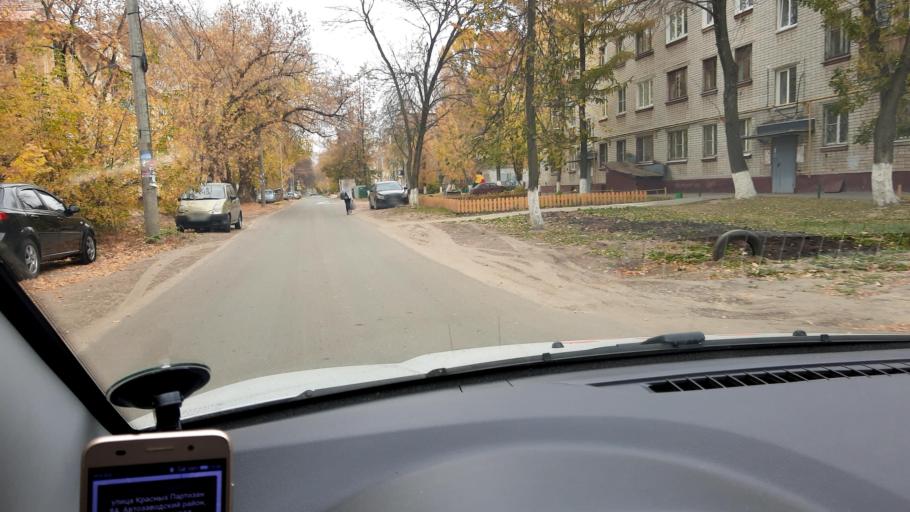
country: RU
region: Nizjnij Novgorod
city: Gorbatovka
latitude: 56.2423
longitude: 43.8372
